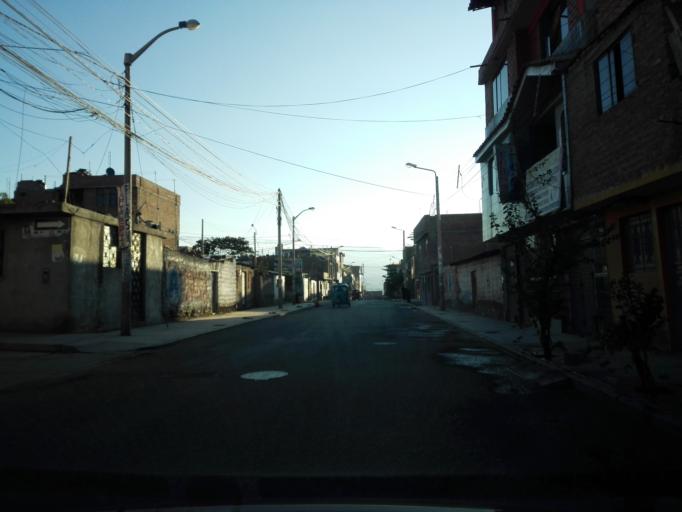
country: PE
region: Ayacucho
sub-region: Provincia de Huamanga
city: Ayacucho
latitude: -13.1508
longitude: -74.2160
